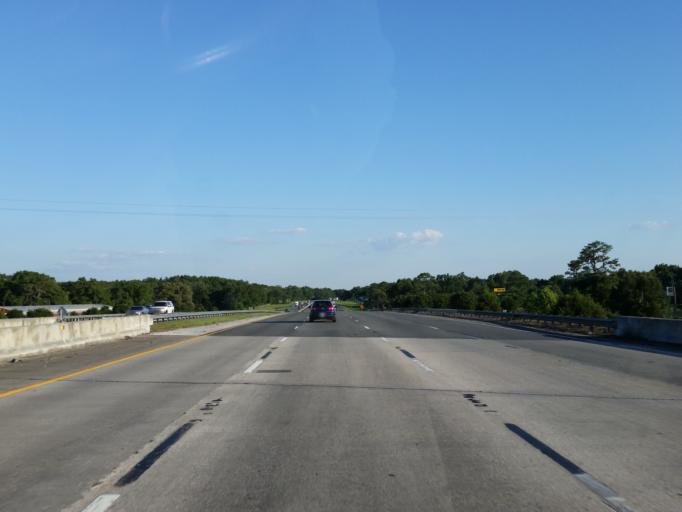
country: US
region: Florida
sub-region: Marion County
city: Ocala
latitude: 29.2671
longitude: -82.1933
